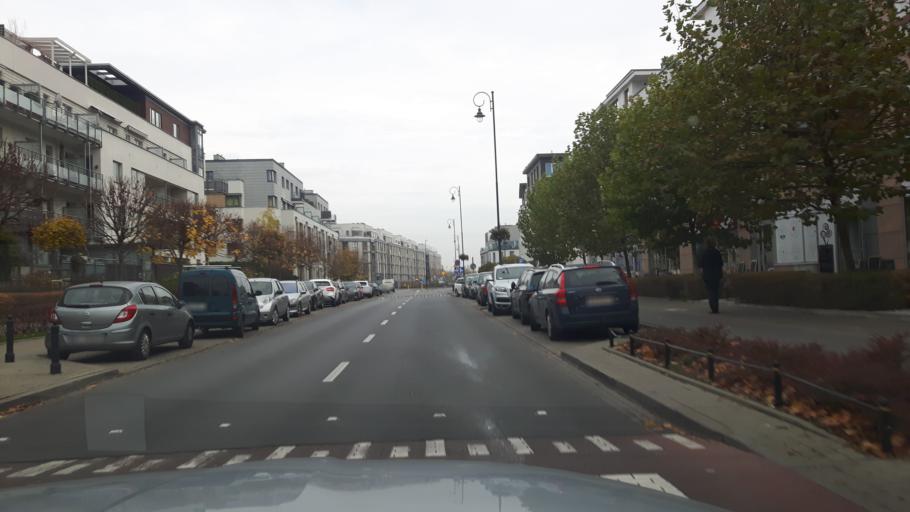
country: PL
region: Masovian Voivodeship
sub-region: Warszawa
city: Wilanow
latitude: 52.1594
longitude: 21.0795
